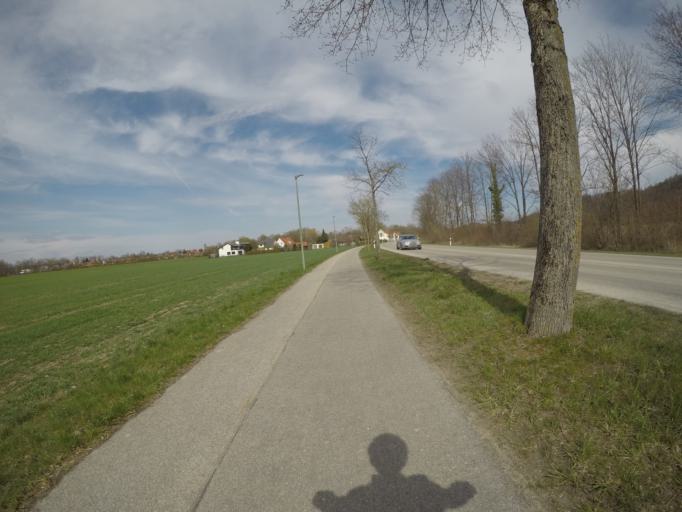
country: DE
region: Bavaria
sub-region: Lower Bavaria
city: Stallwang
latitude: 48.5620
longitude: 12.2022
